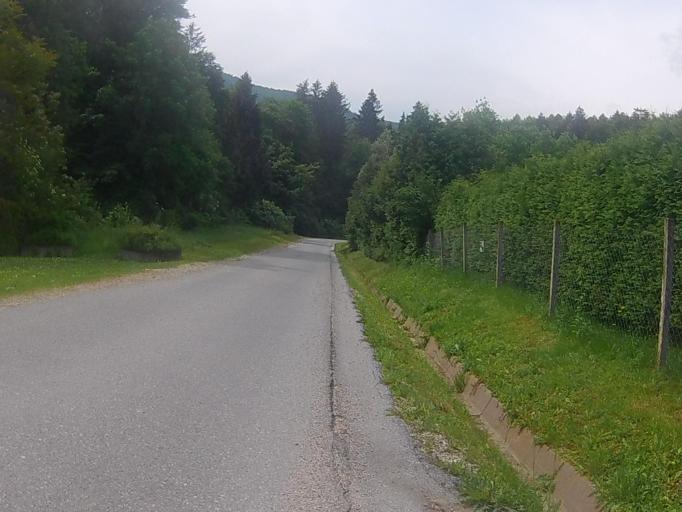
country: SI
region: Maribor
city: Pekre
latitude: 46.5310
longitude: 15.5814
